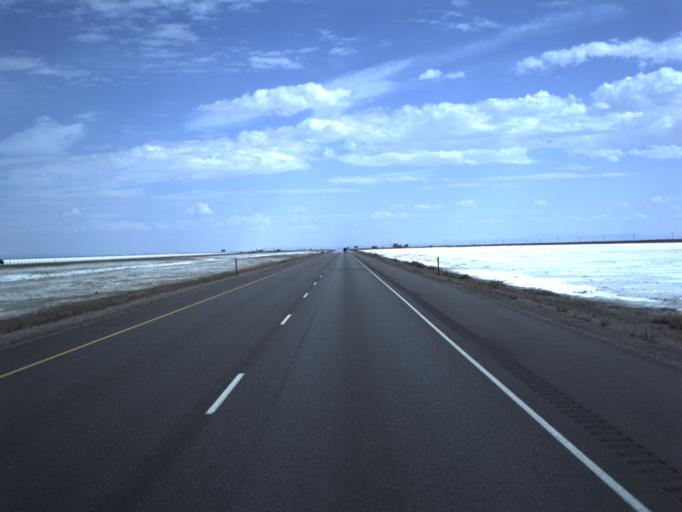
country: US
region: Utah
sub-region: Tooele County
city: Wendover
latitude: 40.7390
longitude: -113.8799
